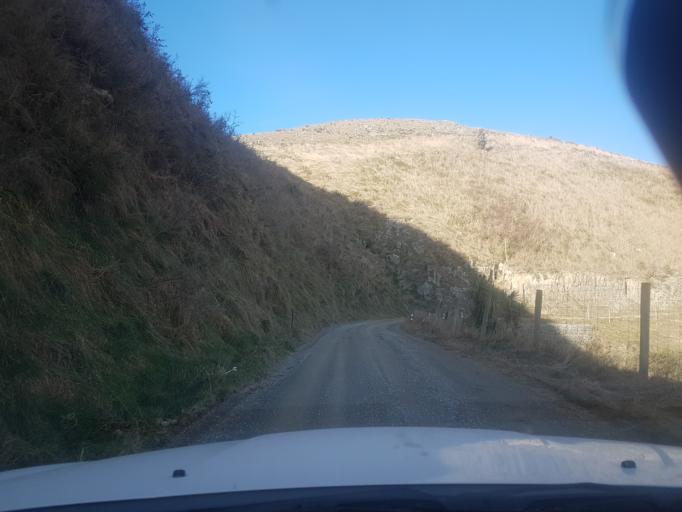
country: NZ
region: Canterbury
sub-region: Timaru District
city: Pleasant Point
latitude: -44.1714
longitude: 170.8835
